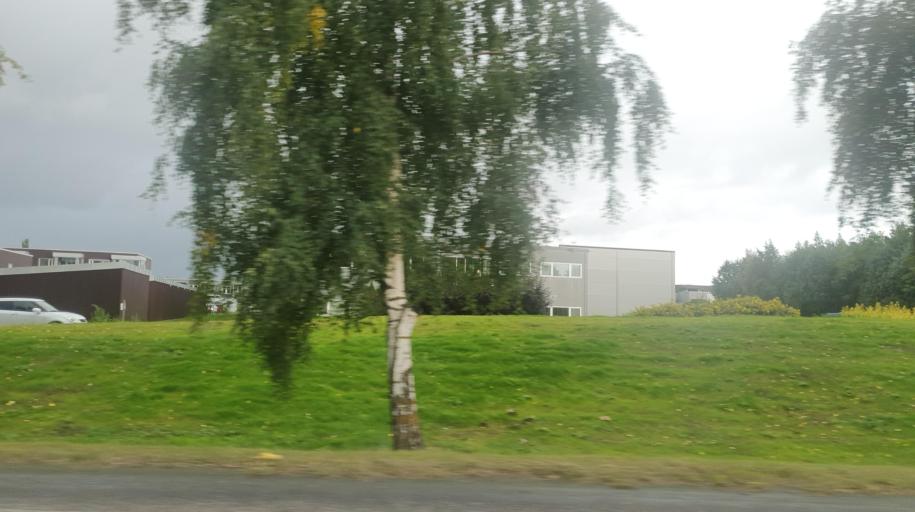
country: NO
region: Nord-Trondelag
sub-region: Verdal
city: Verdal
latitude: 63.7912
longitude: 11.4890
